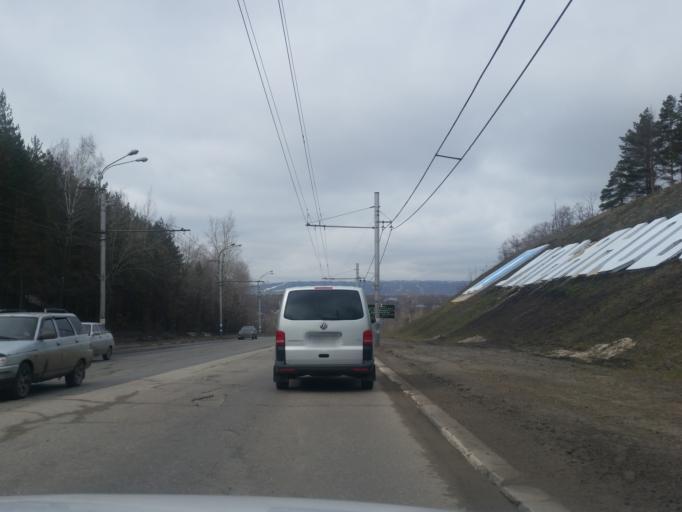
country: RU
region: Ulyanovsk
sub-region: Ulyanovskiy Rayon
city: Ulyanovsk
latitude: 54.3334
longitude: 48.5126
